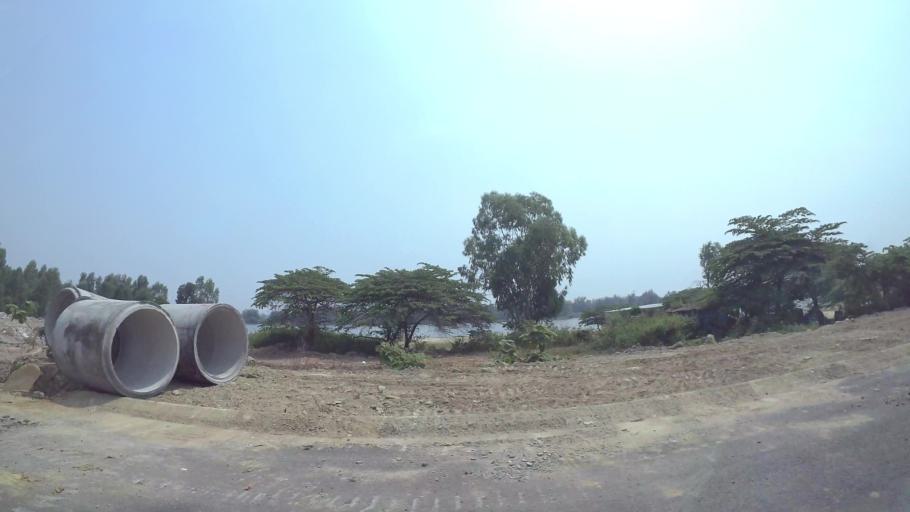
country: VN
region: Da Nang
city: Cam Le
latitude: 15.9797
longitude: 108.2203
